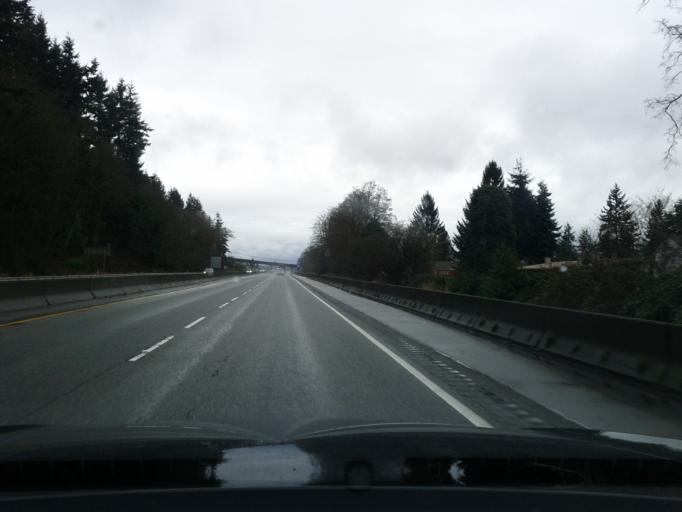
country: US
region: Washington
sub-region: Skagit County
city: Mount Vernon
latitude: 48.4105
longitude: -122.3314
